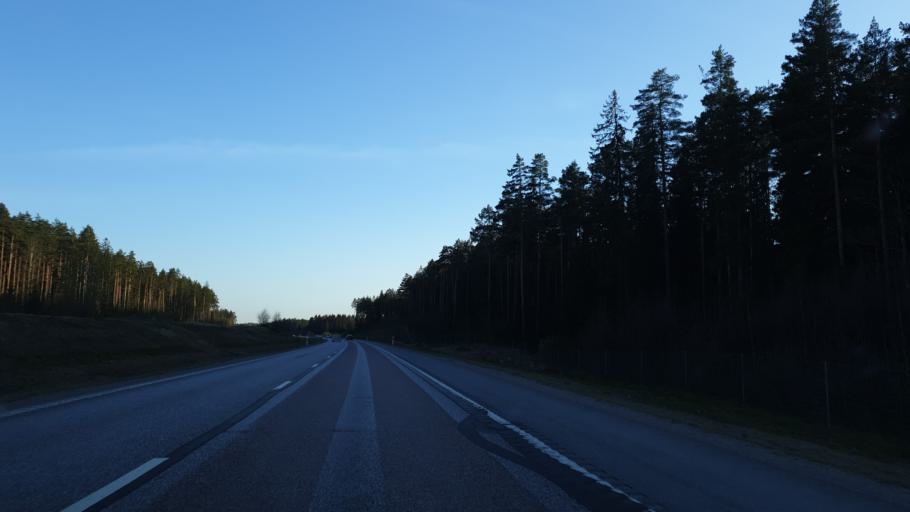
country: SE
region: Uppsala
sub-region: Tierps Kommun
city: Tierp
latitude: 60.2838
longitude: 17.5036
